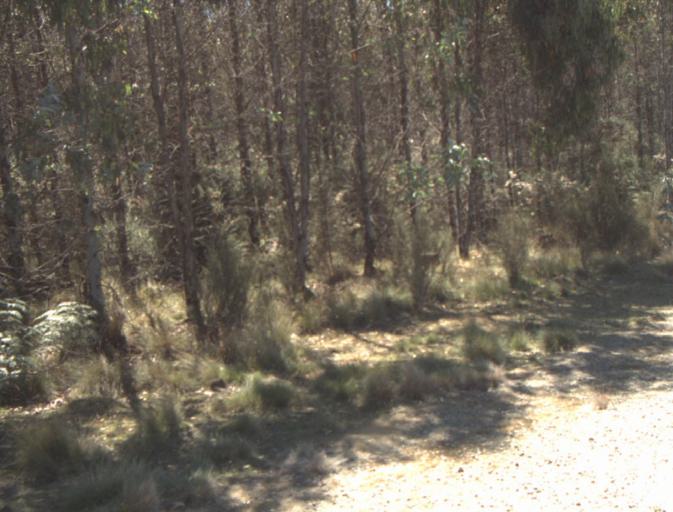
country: AU
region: Tasmania
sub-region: Dorset
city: Scottsdale
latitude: -41.3046
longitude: 147.4675
